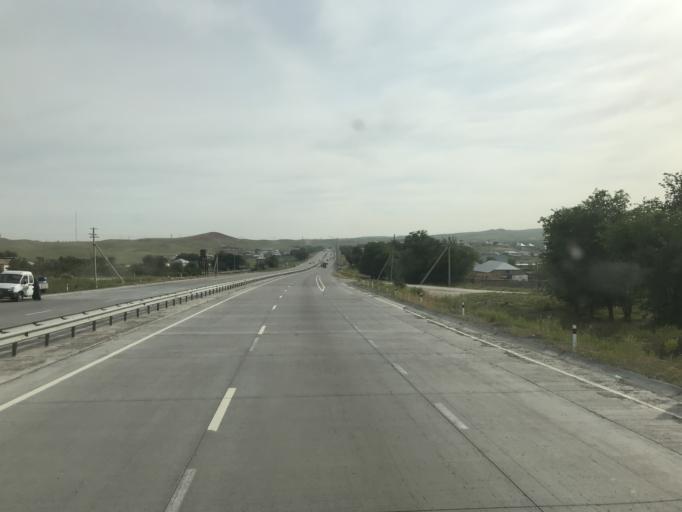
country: KZ
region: Ongtustik Qazaqstan
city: Shymkent
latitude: 42.2082
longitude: 69.5153
